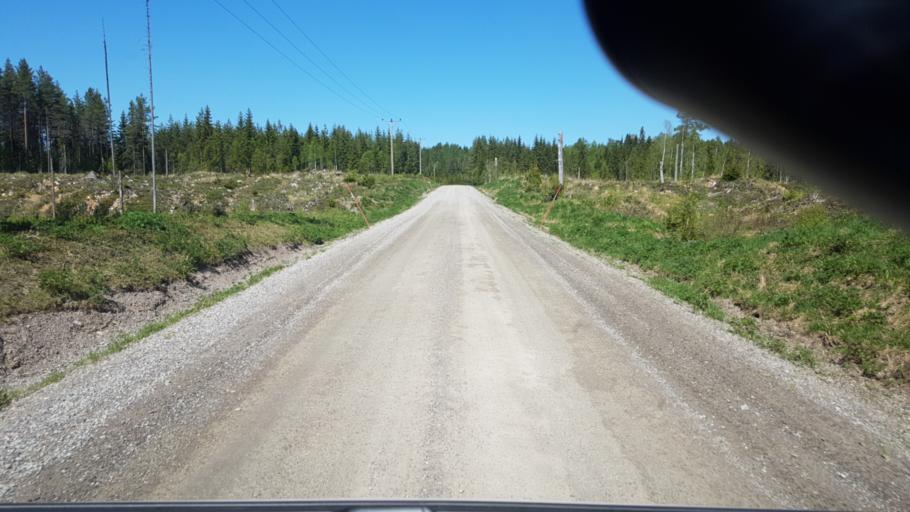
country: SE
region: Vaermland
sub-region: Arvika Kommun
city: Arvika
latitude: 59.8664
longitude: 12.7125
